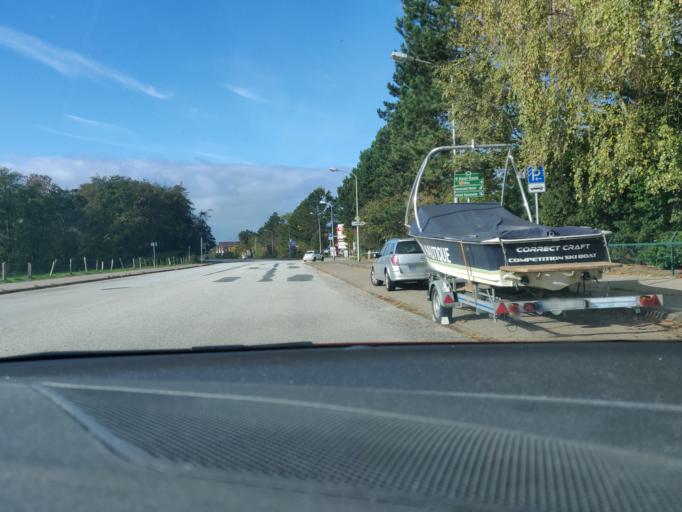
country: DE
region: Lower Saxony
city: Cuxhaven
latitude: 53.8839
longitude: 8.6647
